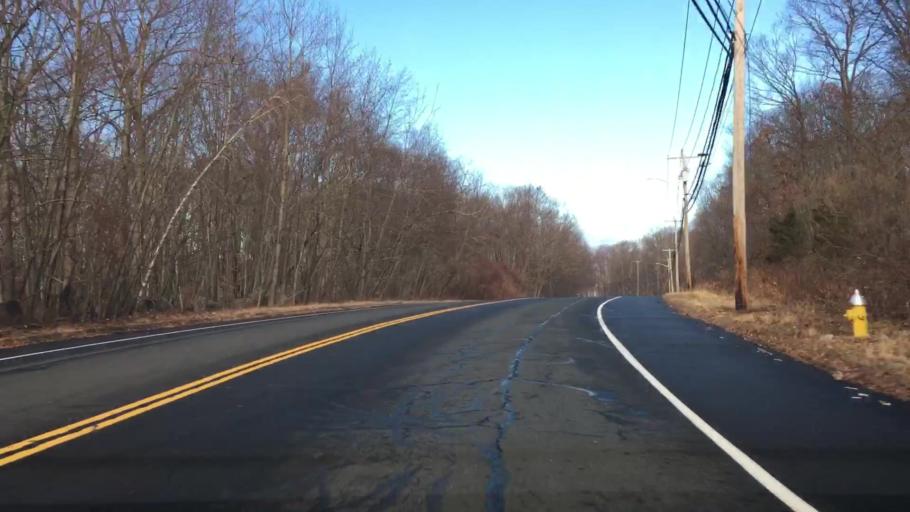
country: US
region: Connecticut
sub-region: Fairfield County
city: Shelton
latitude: 41.2983
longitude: -73.0927
